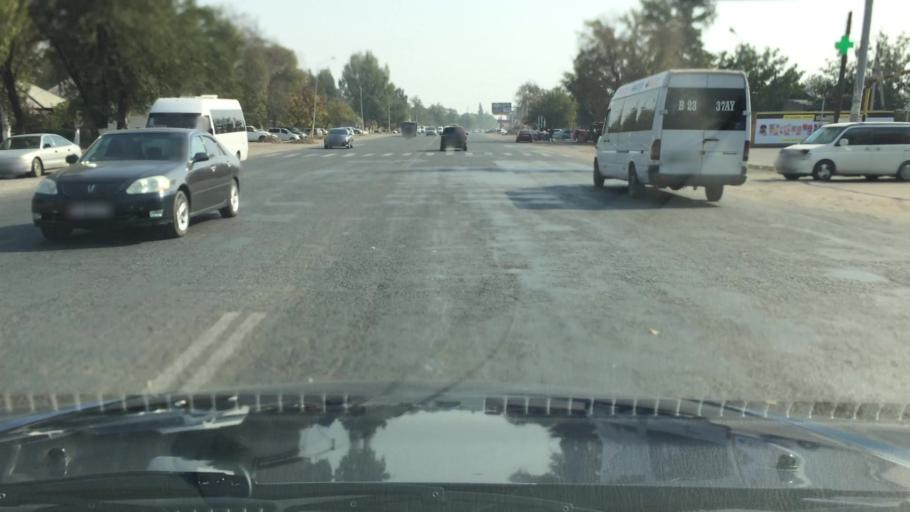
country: KG
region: Chuy
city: Lebedinovka
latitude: 42.8879
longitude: 74.6641
